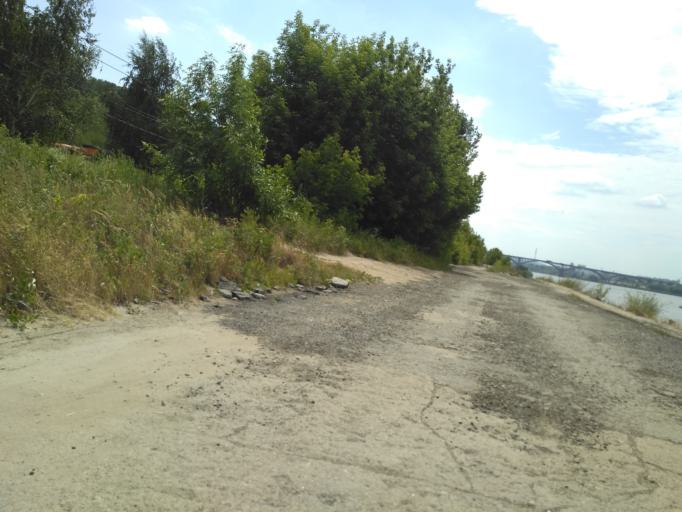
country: RU
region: Nizjnij Novgorod
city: Nizhniy Novgorod
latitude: 56.3156
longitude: 43.9693
